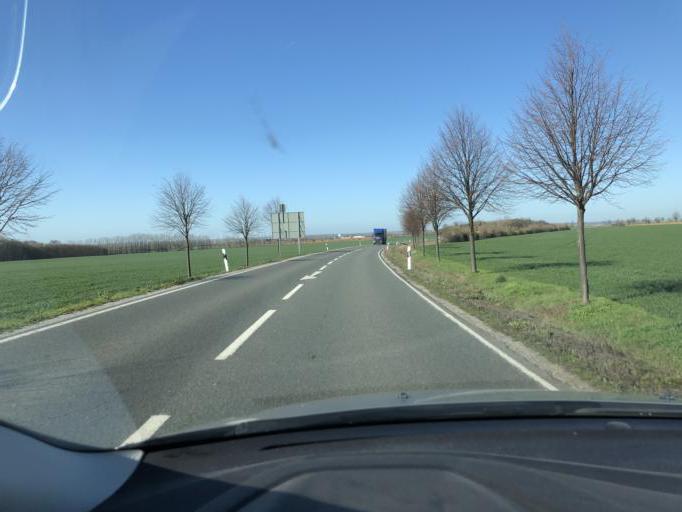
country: DE
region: Saxony-Anhalt
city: Ilberstedt
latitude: 51.8472
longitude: 11.6561
